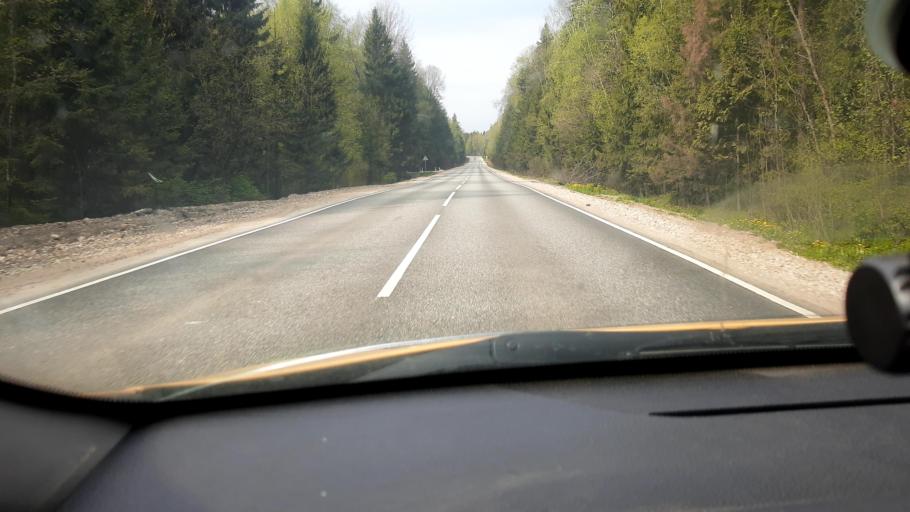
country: RU
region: Moskovskaya
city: Novopetrovskoye
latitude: 55.8116
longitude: 36.3892
